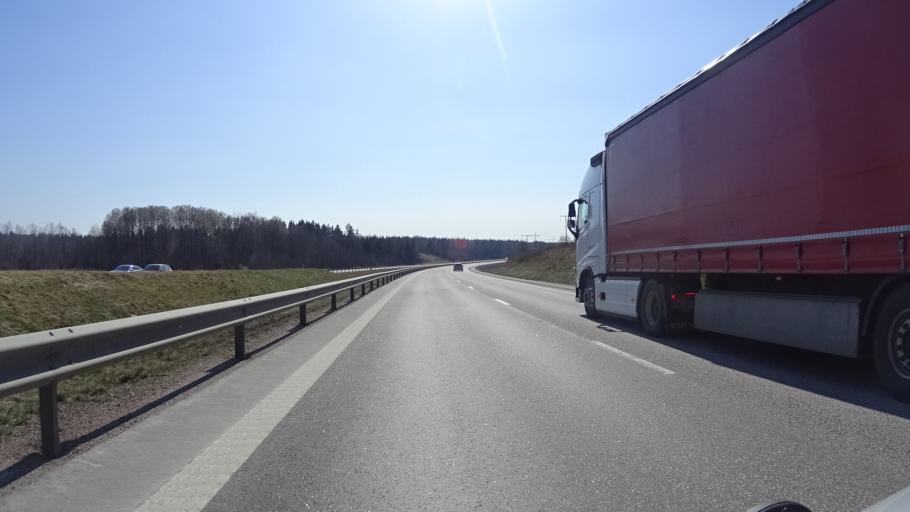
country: SE
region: OEstergoetland
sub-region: Vadstena Kommun
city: Herrestad
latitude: 58.2732
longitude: 14.8636
